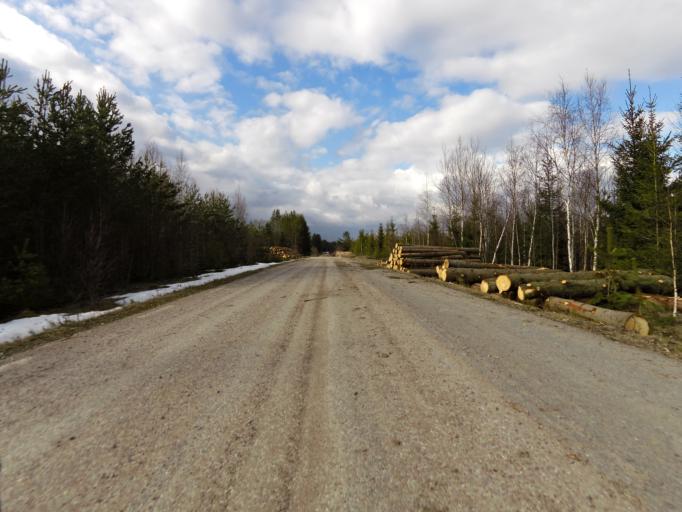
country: SE
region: Gaevleborg
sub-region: Hofors Kommun
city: Hofors
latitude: 60.4766
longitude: 16.4523
